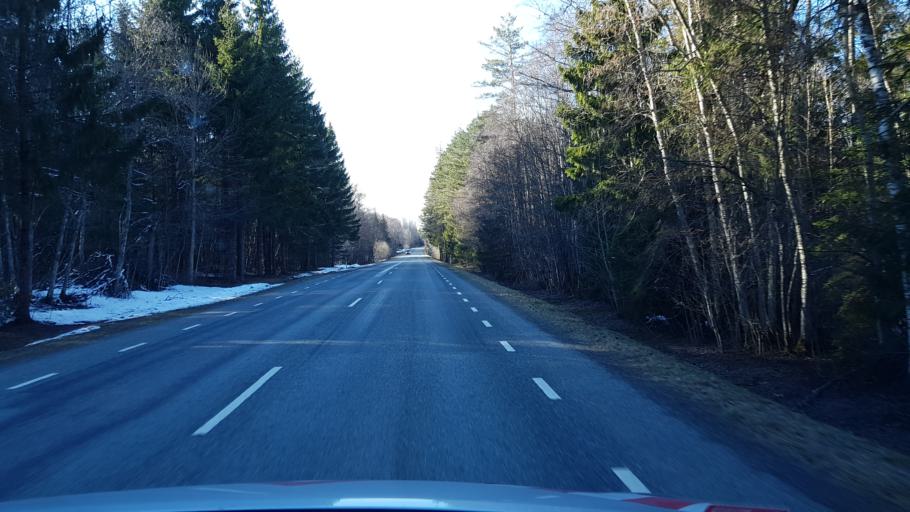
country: EE
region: Laeaene-Virumaa
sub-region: Tapa vald
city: Tapa
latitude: 59.4322
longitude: 25.9706
